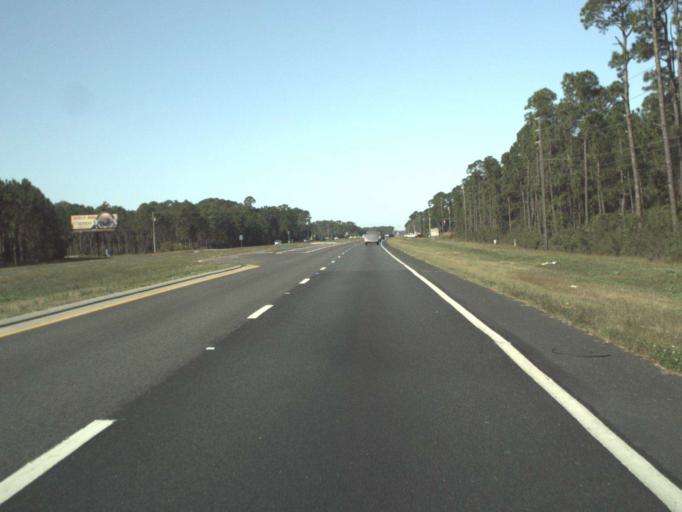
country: US
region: Florida
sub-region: Walton County
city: Miramar Beach
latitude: 30.3745
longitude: -86.2476
